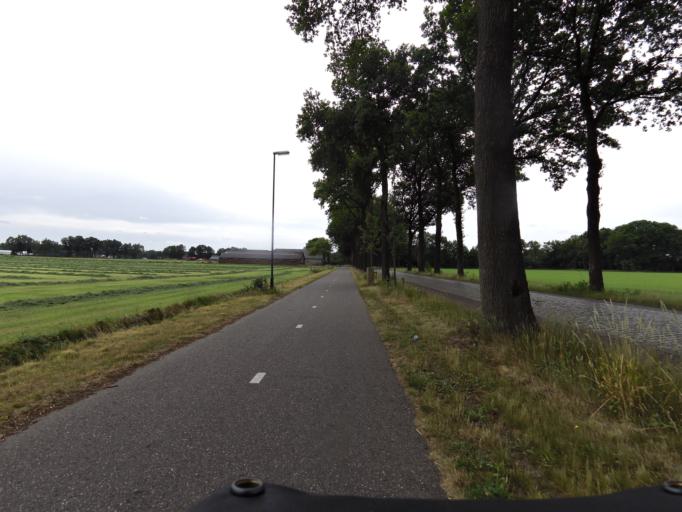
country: NL
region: North Brabant
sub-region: Gemeente Bladel en Netersel
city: Bladel
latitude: 51.3858
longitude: 5.2120
